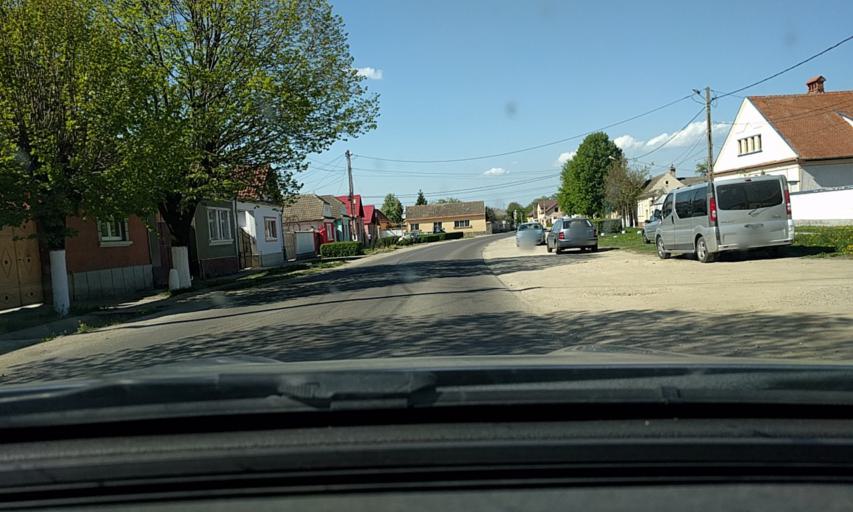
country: RO
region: Brasov
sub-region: Comuna Harman
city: Harman
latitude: 45.7111
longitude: 25.6847
